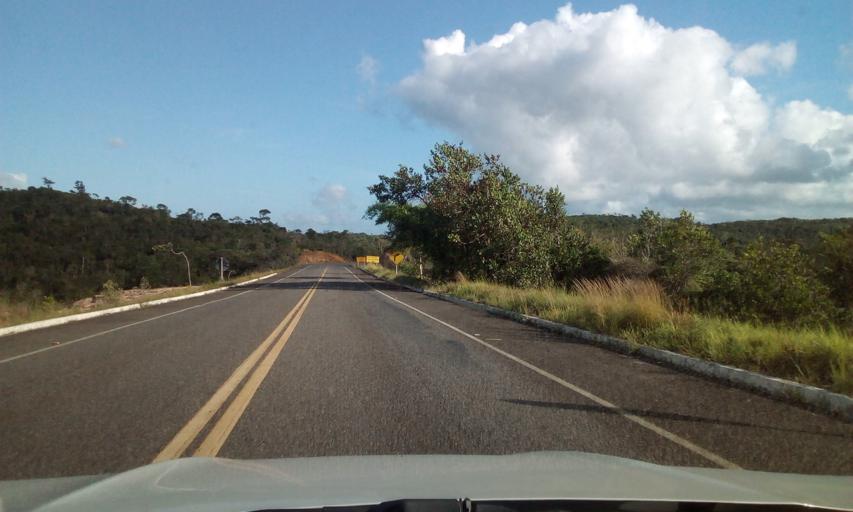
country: BR
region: Bahia
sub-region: Conde
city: Conde
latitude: -12.0924
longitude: -37.7733
